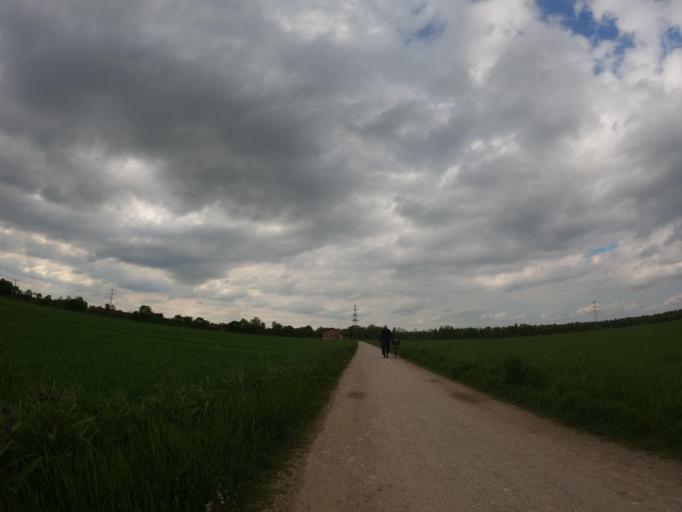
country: DE
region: Bavaria
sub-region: Upper Bavaria
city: Hohenbrunn
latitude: 48.0527
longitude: 11.6955
